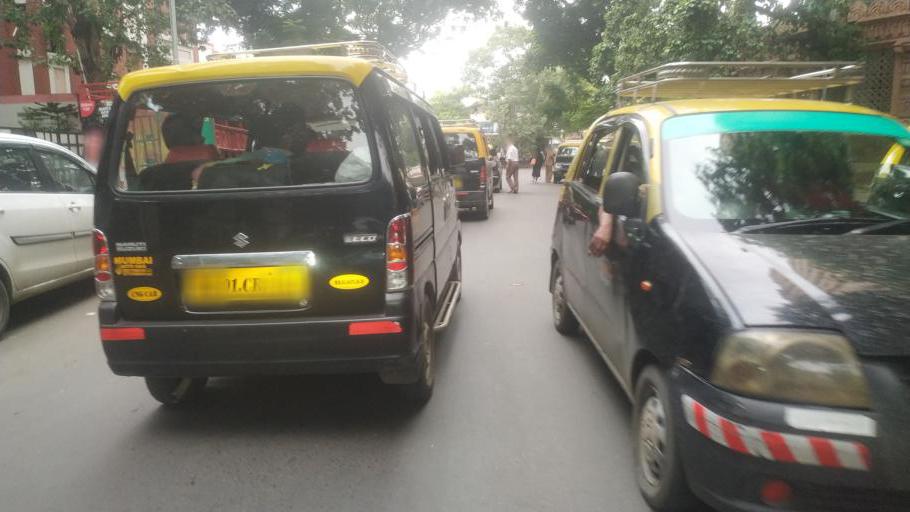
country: IN
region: Maharashtra
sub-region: Mumbai Suburban
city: Mumbai
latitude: 19.0172
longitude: 72.8448
